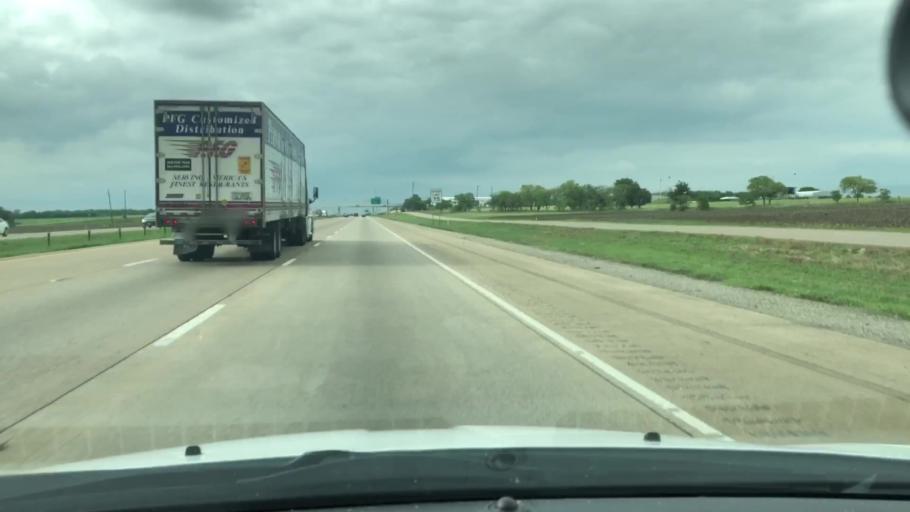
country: US
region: Texas
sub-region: Ellis County
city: Ennis
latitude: 32.3454
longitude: -96.6218
